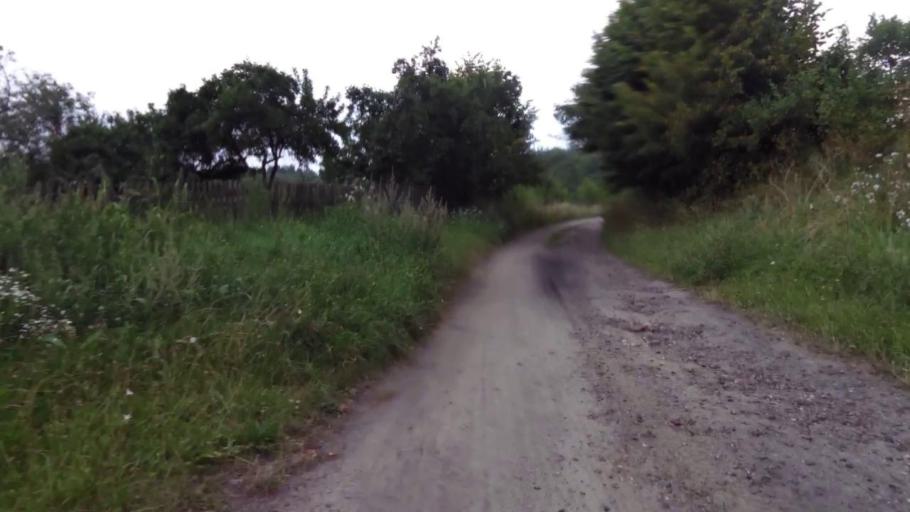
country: PL
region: West Pomeranian Voivodeship
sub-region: Powiat lobeski
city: Lobez
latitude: 53.5392
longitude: 15.6748
